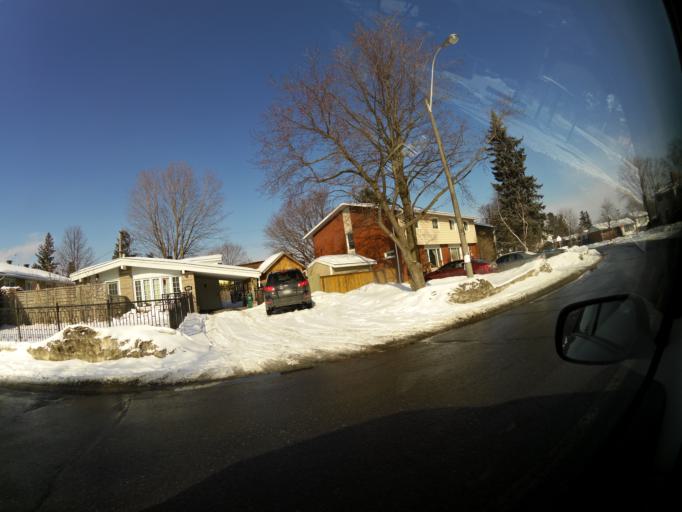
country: CA
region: Ontario
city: Ottawa
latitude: 45.3893
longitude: -75.6267
